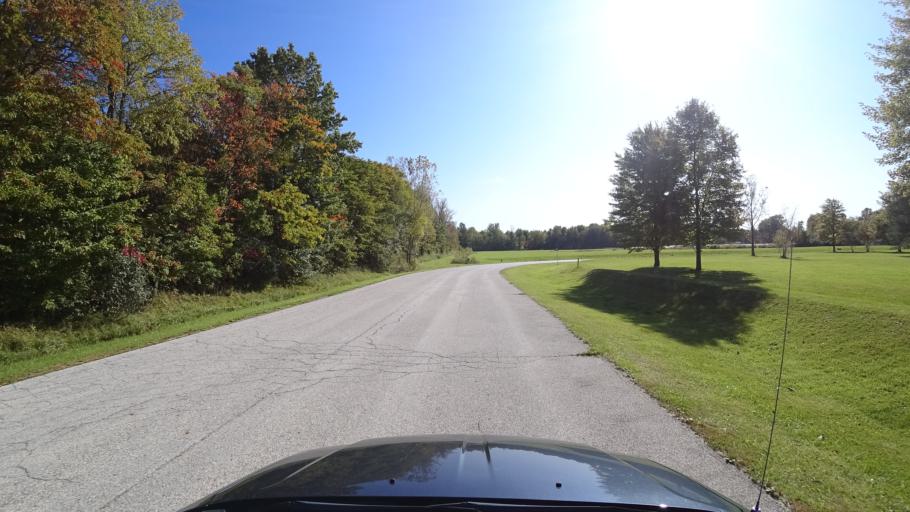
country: US
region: Indiana
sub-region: LaPorte County
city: Trail Creek
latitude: 41.6974
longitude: -86.8356
